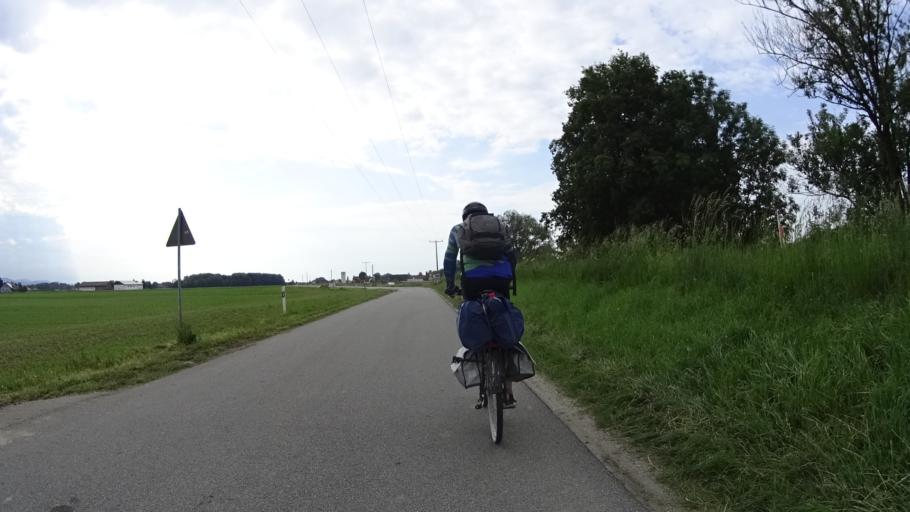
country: DE
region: Bavaria
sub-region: Lower Bavaria
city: Irlbach
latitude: 48.8698
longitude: 12.7584
